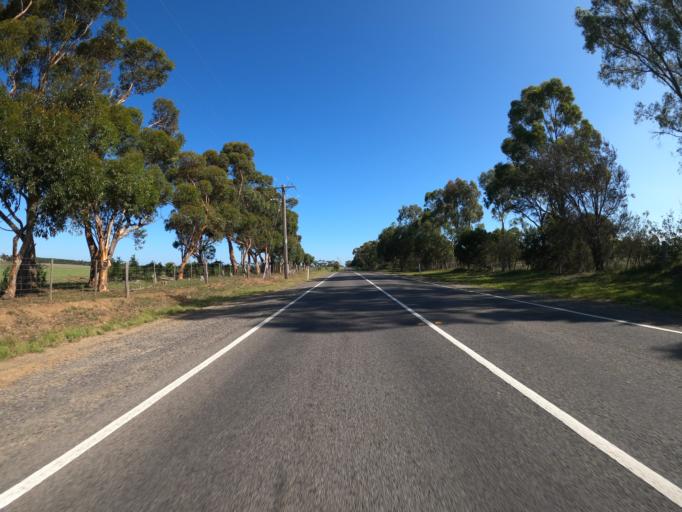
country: AU
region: Victoria
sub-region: Hume
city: Greenvale
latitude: -37.5678
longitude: 144.8472
